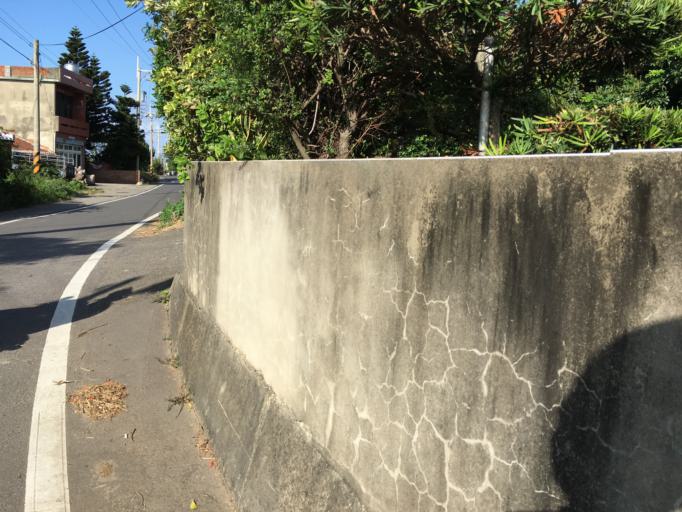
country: TW
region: Taiwan
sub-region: Hsinchu
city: Zhubei
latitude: 24.9254
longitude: 120.9841
